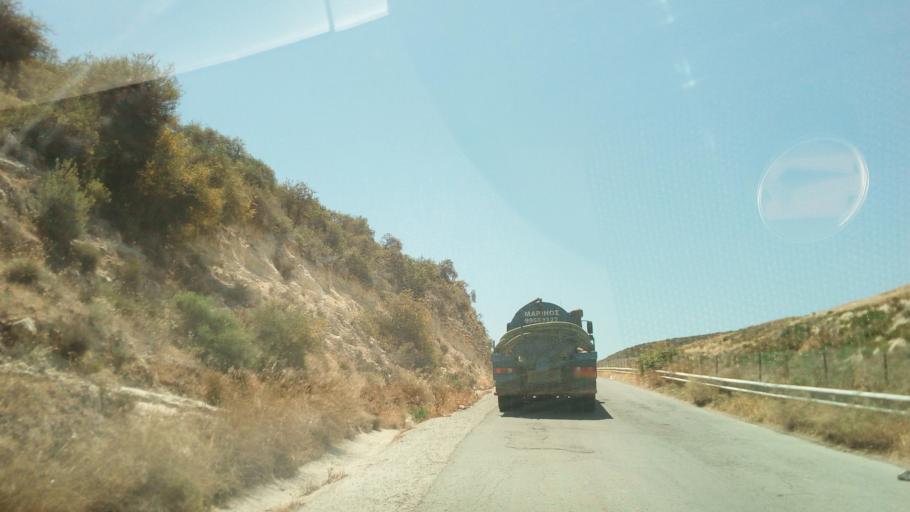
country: CY
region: Limassol
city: Pano Polemidia
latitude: 34.7506
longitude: 32.9537
